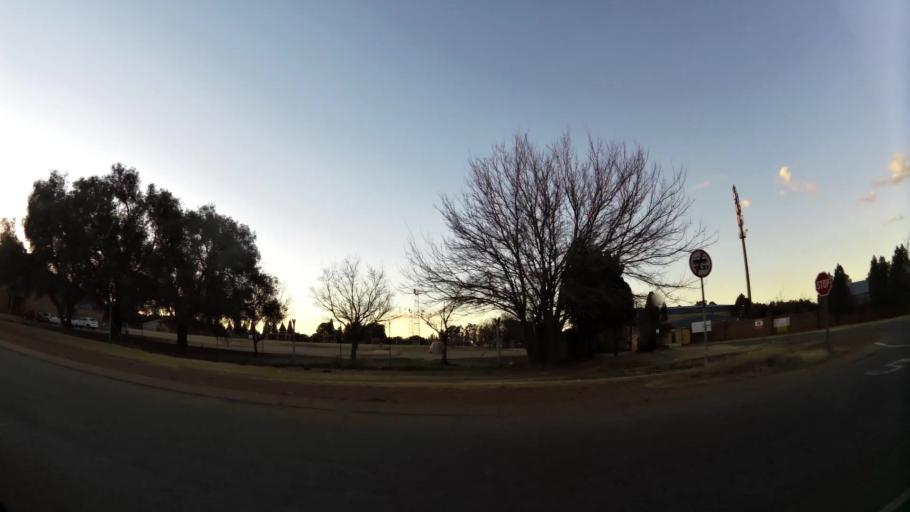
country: ZA
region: North-West
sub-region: Dr Kenneth Kaunda District Municipality
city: Potchefstroom
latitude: -26.6889
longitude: 27.0811
